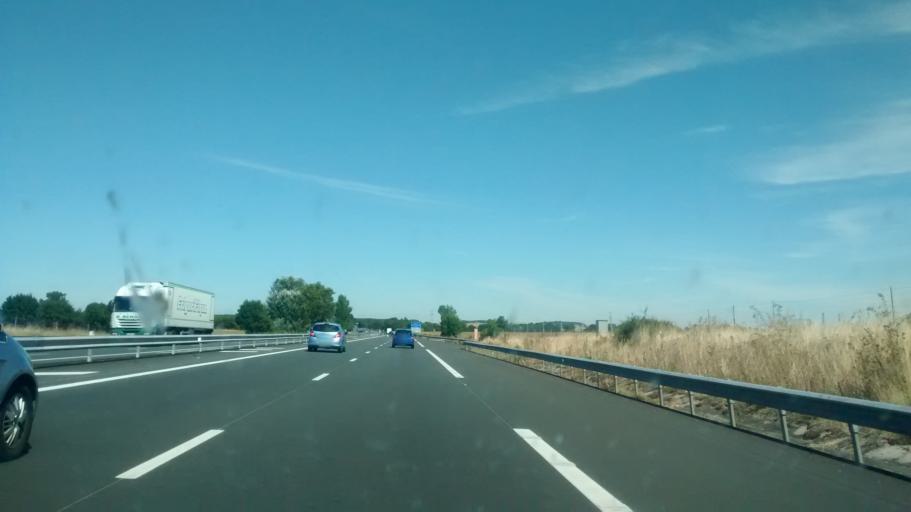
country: FR
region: Poitou-Charentes
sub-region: Departement des Deux-Sevres
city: Beauvoir-sur-Niort
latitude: 46.1482
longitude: -0.5217
